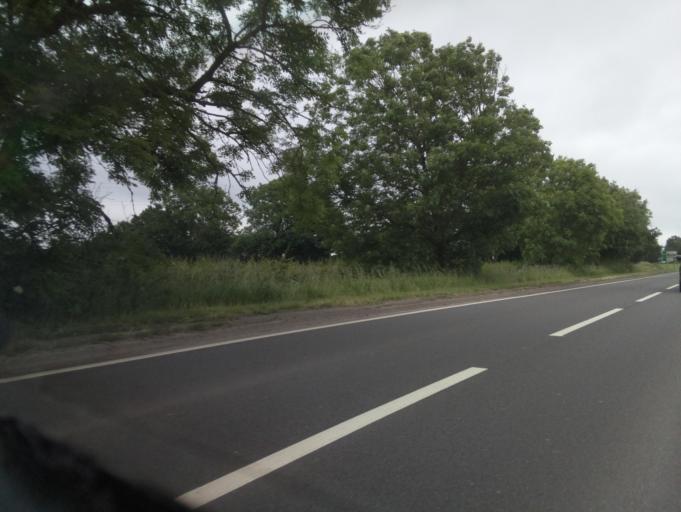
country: GB
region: England
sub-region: Derbyshire
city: Yeldersley
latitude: 52.9632
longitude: -1.6026
